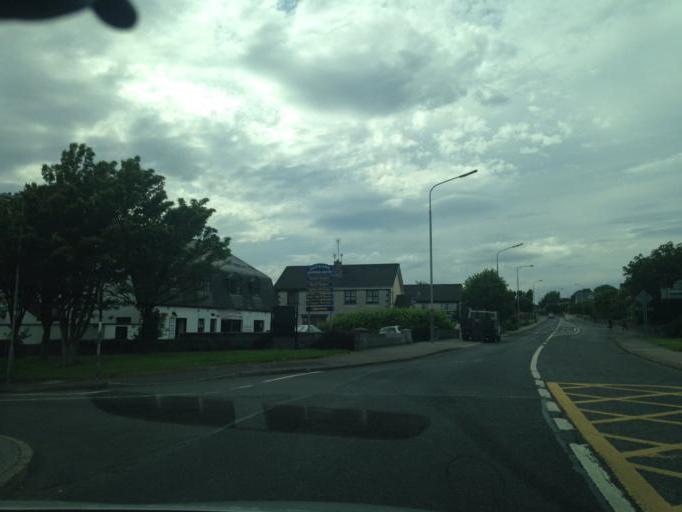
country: IE
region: Connaught
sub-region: County Galway
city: Gaillimh
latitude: 53.2872
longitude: -9.0463
